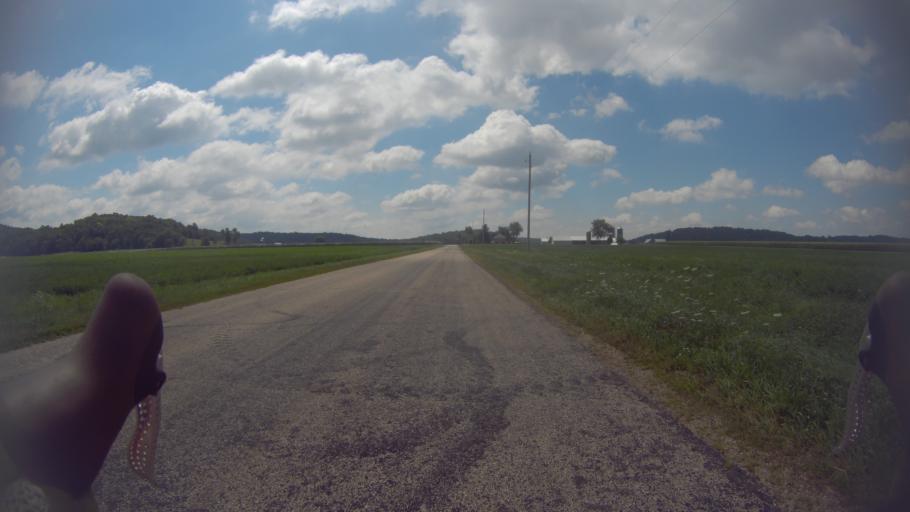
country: US
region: Wisconsin
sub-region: Sauk County
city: Sauk City
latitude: 43.2275
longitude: -89.6405
